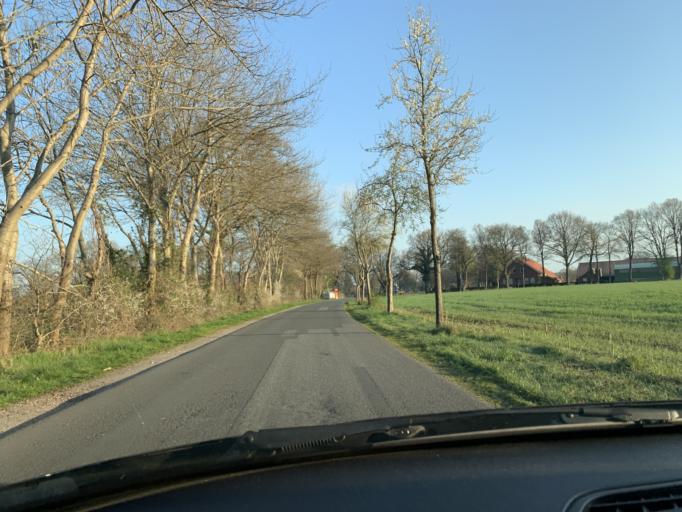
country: DE
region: Lower Saxony
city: Apen
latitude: 53.2926
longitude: 7.8074
